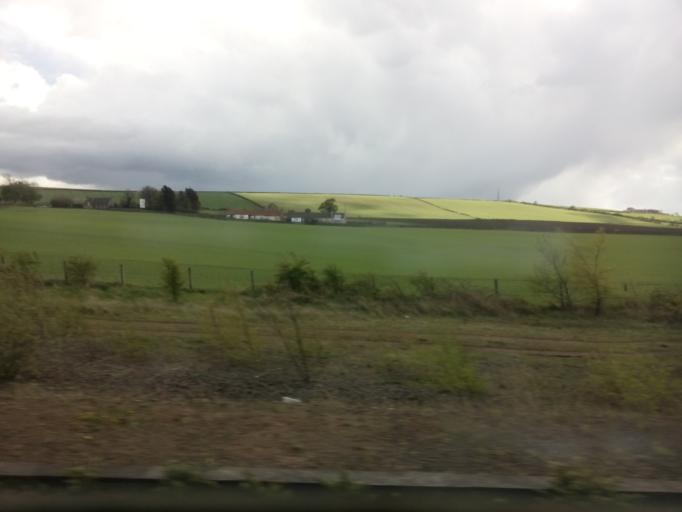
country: GB
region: Scotland
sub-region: East Lothian
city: Prestonpans
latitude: 55.9466
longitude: -2.9949
